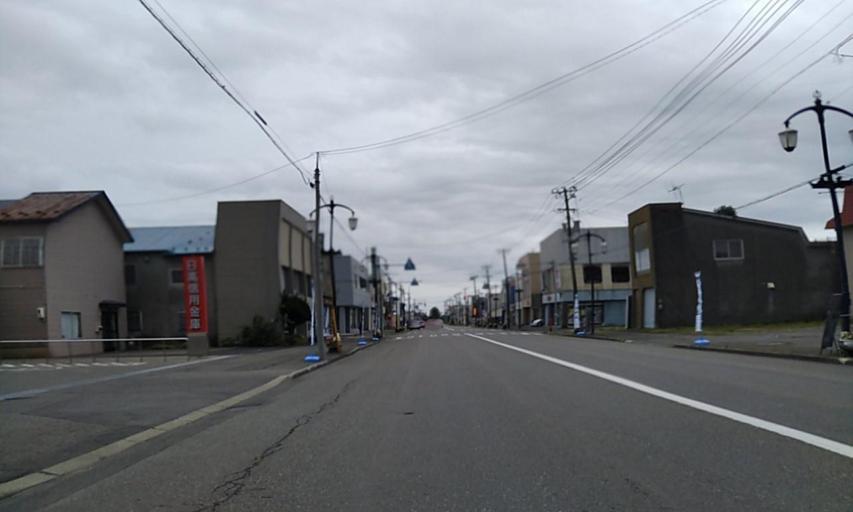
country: JP
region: Hokkaido
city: Obihiro
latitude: 42.2885
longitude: 143.3156
